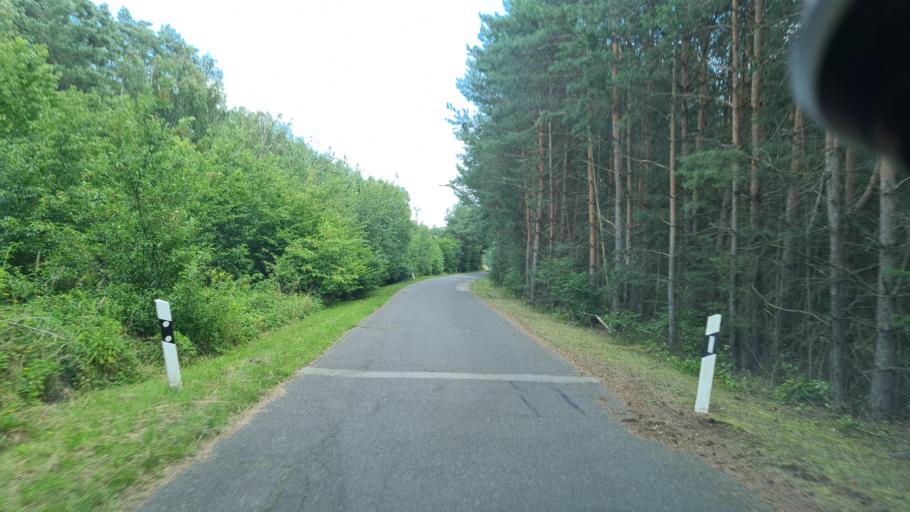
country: DE
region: Brandenburg
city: Drebkau
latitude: 51.6202
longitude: 14.2601
